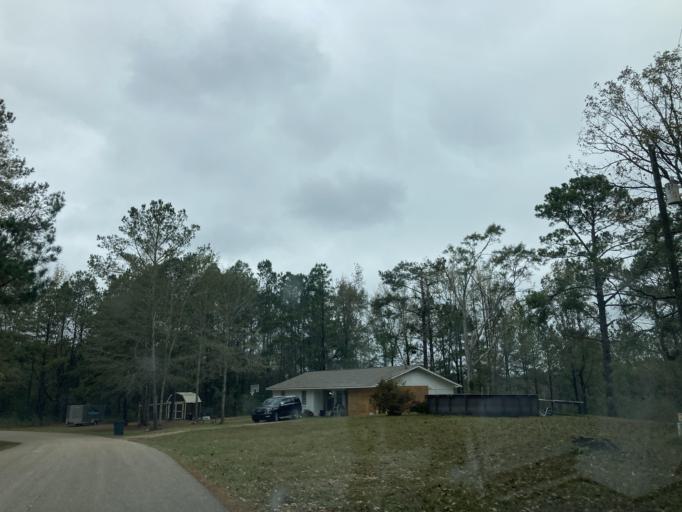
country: US
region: Mississippi
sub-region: Lamar County
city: Purvis
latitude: 31.2474
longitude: -89.5029
